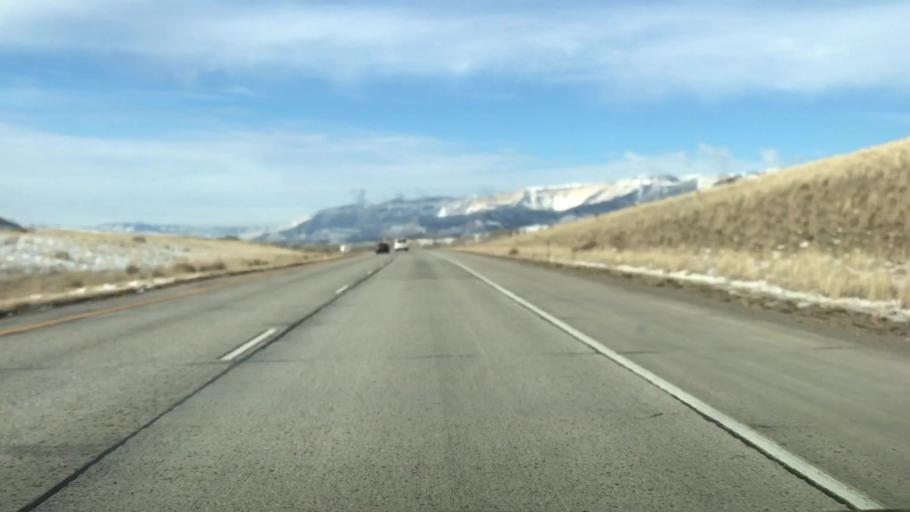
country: US
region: Colorado
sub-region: Garfield County
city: Rifle
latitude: 39.5308
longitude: -107.7355
